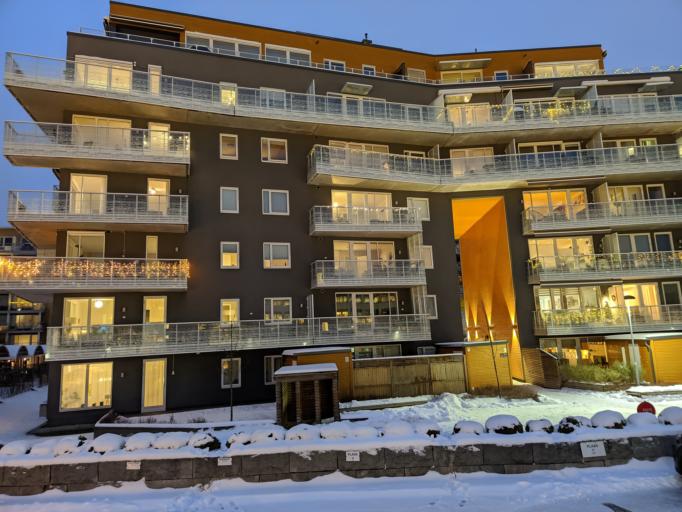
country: NO
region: Oslo
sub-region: Oslo
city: Oslo
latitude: 59.9421
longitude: 10.7690
